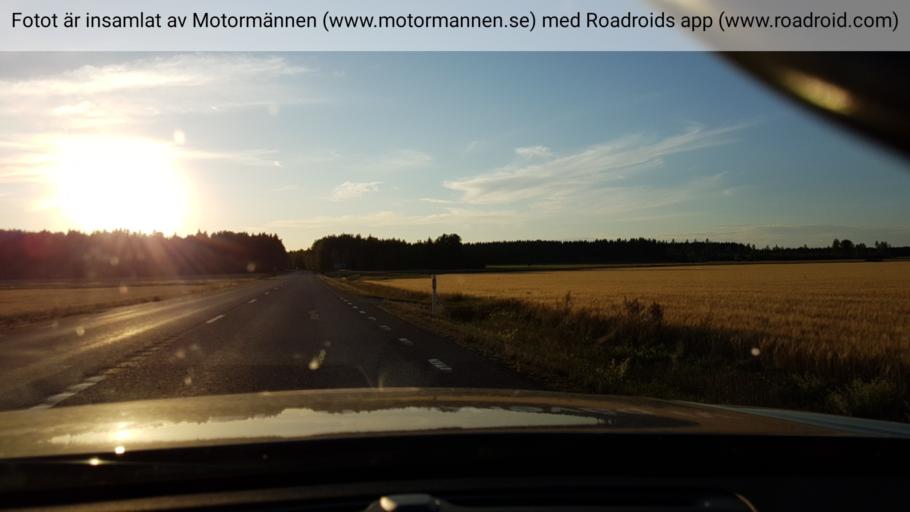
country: SE
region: OErebro
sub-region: Karlskoga Kommun
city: Karlskoga
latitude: 59.3790
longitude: 14.4968
